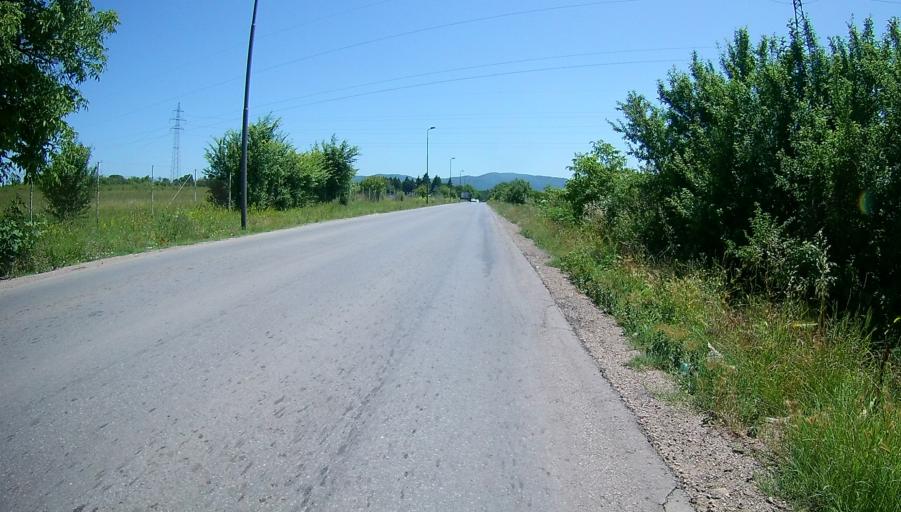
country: RS
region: Central Serbia
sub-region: Nisavski Okrug
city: Nis
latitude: 43.2978
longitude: 21.8783
